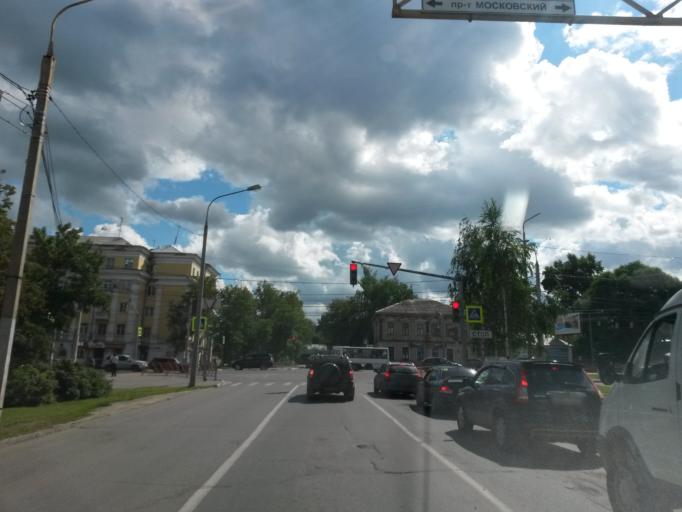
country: RU
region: Jaroslavl
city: Yaroslavl
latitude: 57.6054
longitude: 39.8776
